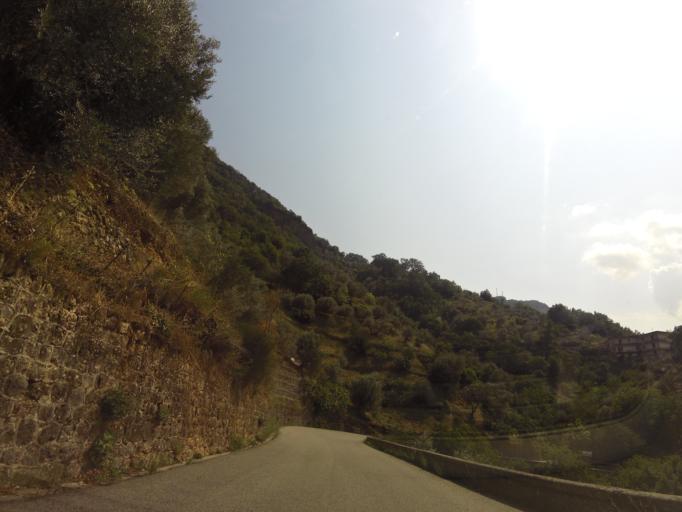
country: IT
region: Calabria
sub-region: Provincia di Reggio Calabria
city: Bivongi
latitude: 38.4811
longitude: 16.4553
